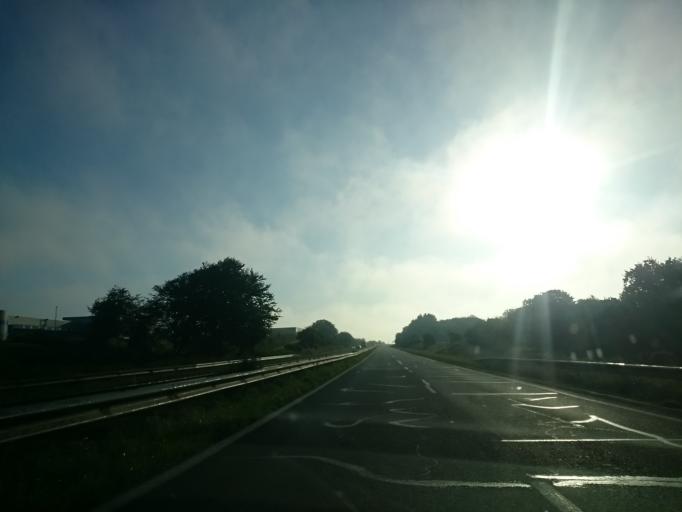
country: FR
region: Brittany
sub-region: Departement du Finistere
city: Guipavas
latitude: 48.4364
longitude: -4.4275
